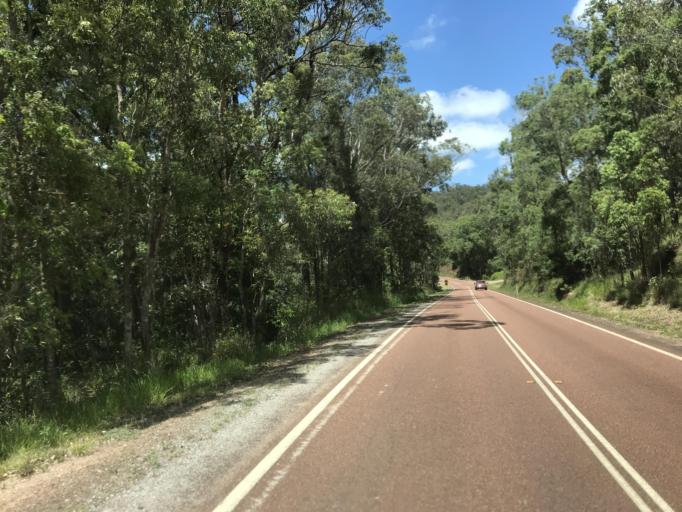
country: AU
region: Queensland
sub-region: Tablelands
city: Ravenshoe
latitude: -17.5988
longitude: 145.4773
